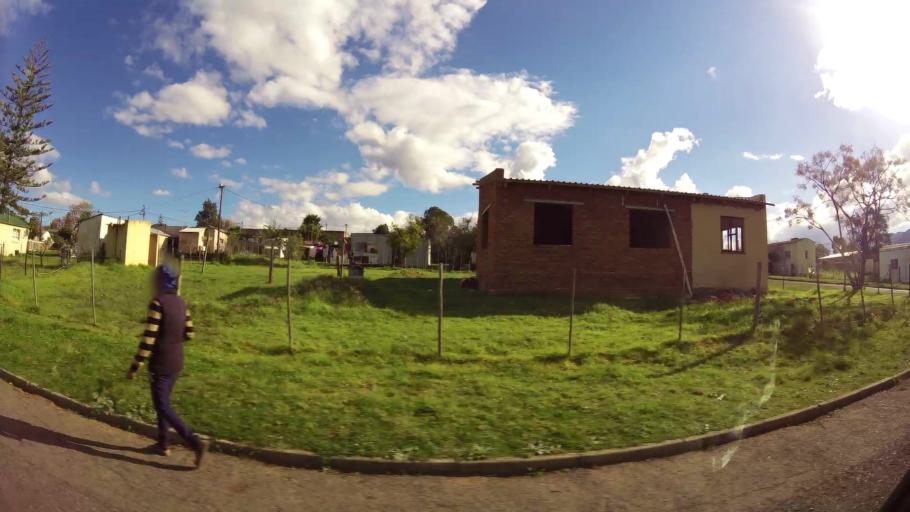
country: ZA
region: Western Cape
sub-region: Overberg District Municipality
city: Swellendam
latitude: -34.0334
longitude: 20.4483
